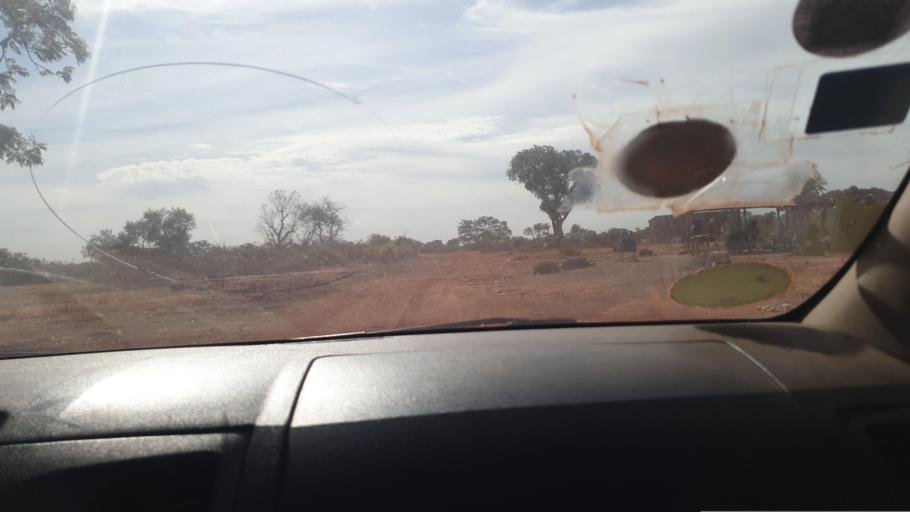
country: ML
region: Sikasso
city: Sikasso
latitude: 11.7732
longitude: -5.9774
